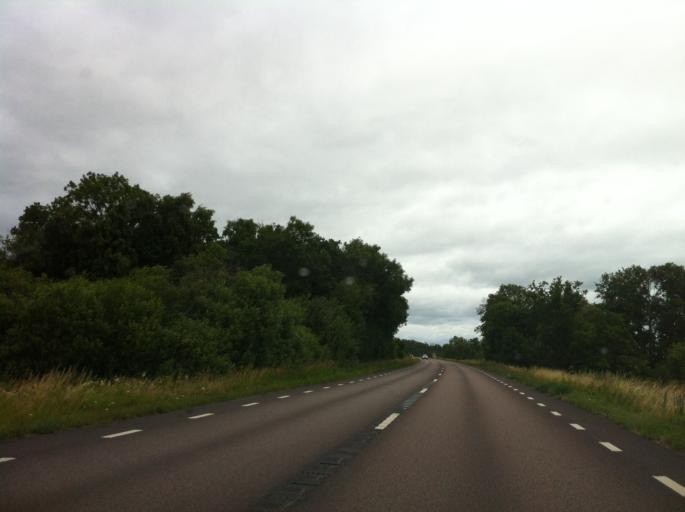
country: SE
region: Kalmar
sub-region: Borgholms Kommun
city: Borgholm
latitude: 57.0767
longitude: 16.9131
